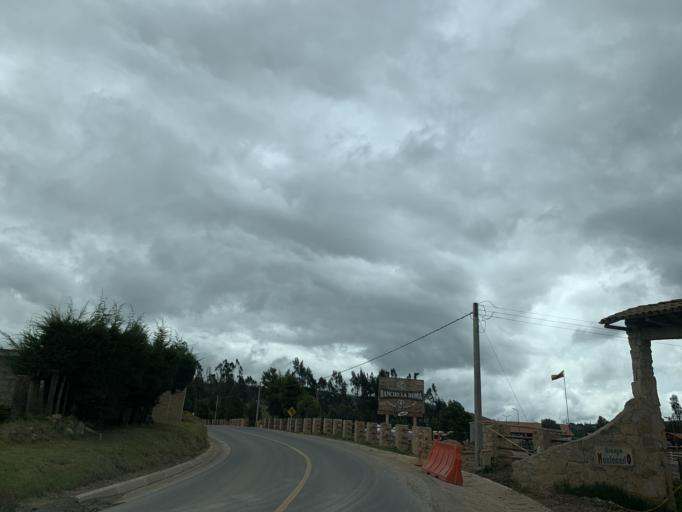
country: CO
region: Boyaca
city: Tunja
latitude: 5.5291
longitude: -73.3319
